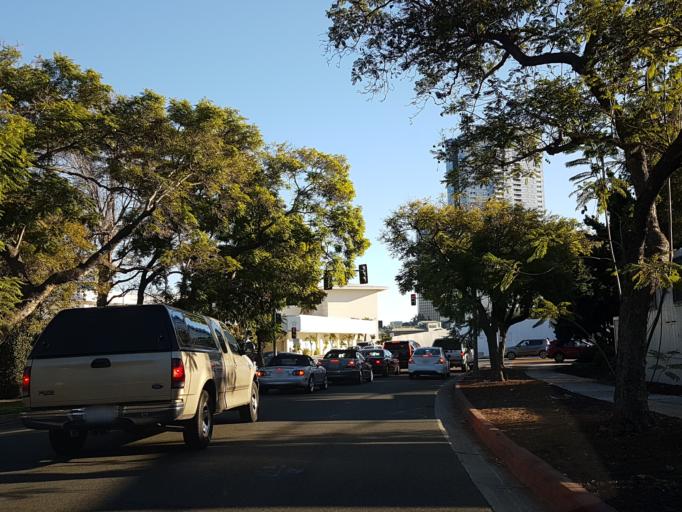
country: US
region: California
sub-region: Los Angeles County
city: Century City
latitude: 34.0677
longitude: -118.4148
